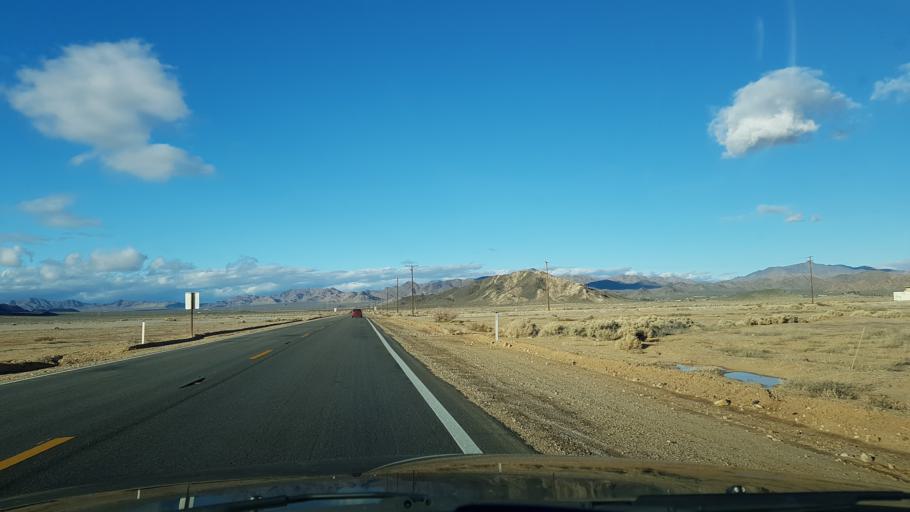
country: US
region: California
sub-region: San Bernardino County
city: Lucerne Valley
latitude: 34.5196
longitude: -116.9452
